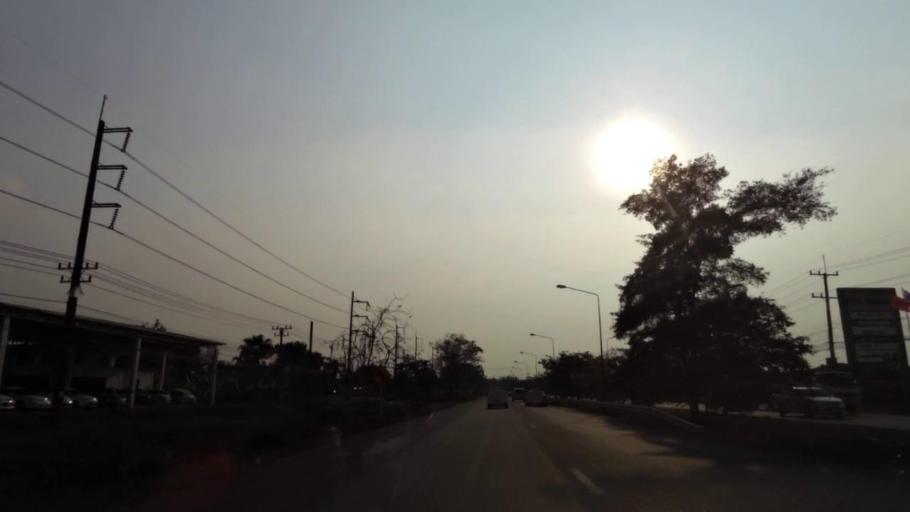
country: TH
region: Chanthaburi
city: Chanthaburi
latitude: 12.6105
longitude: 102.1358
